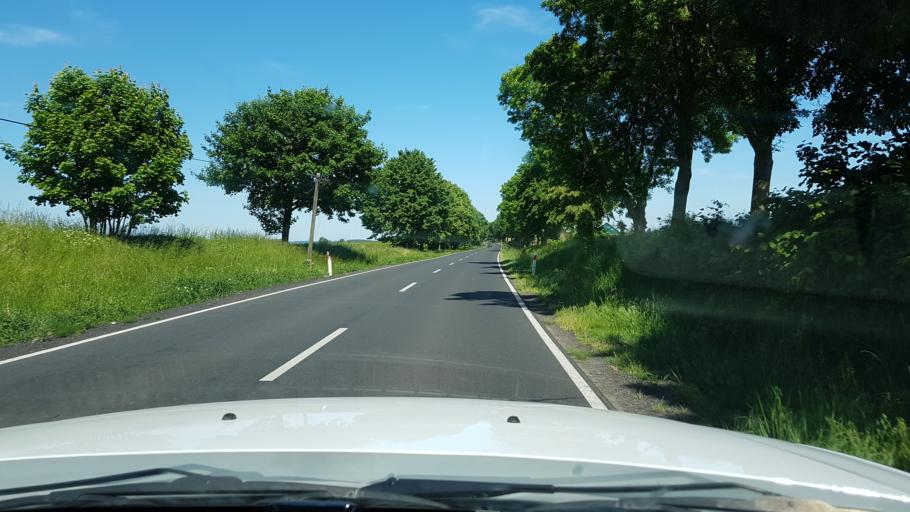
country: PL
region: West Pomeranian Voivodeship
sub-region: Powiat gryfinski
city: Banie
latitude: 53.1106
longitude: 14.6991
